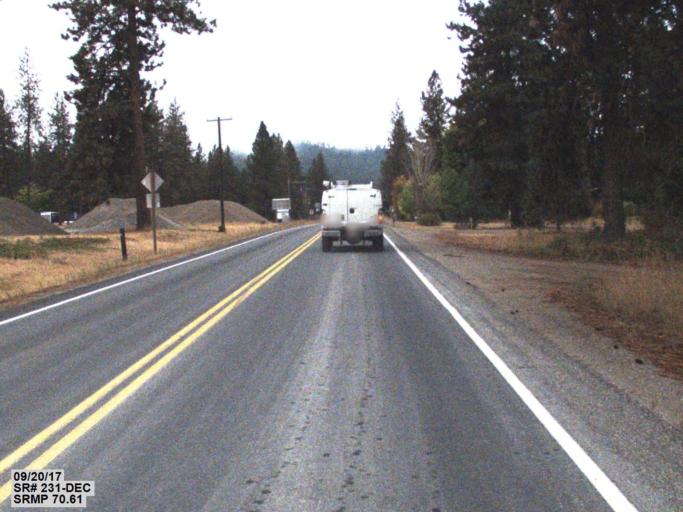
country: US
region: Washington
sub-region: Stevens County
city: Chewelah
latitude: 48.1589
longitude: -117.7258
